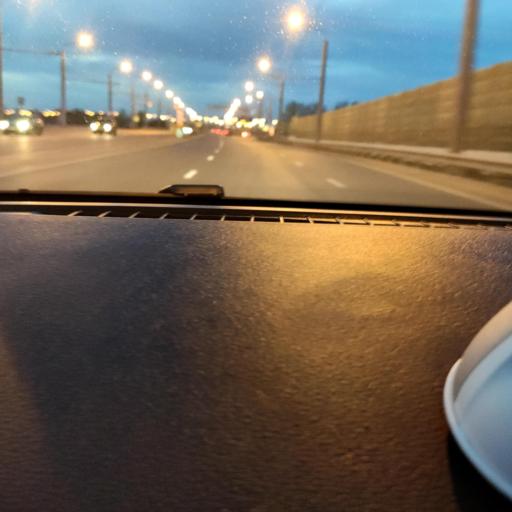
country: RU
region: Samara
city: Samara
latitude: 53.1596
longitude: 50.0907
